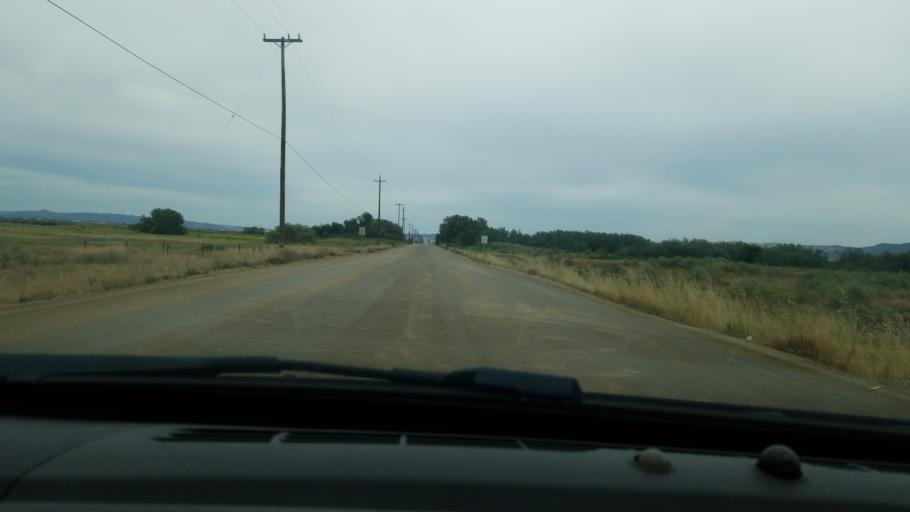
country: US
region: California
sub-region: Santa Barbara County
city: Guadalupe
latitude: 34.9838
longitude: -120.5132
